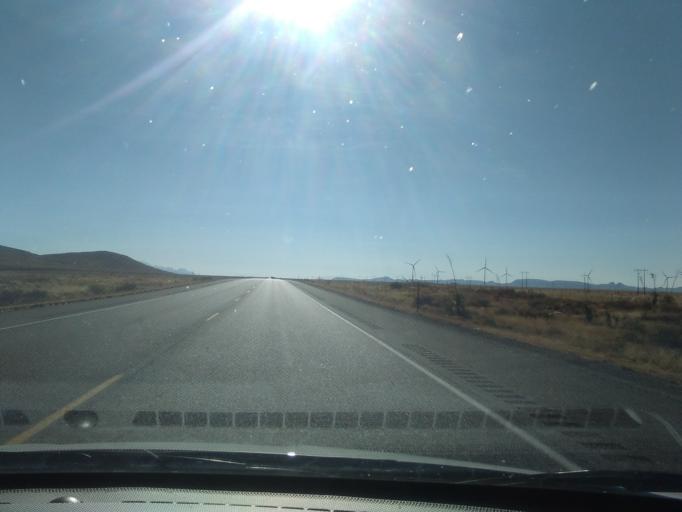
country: US
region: New Mexico
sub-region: Dona Ana County
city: Hatch
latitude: 32.5577
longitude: -107.4725
